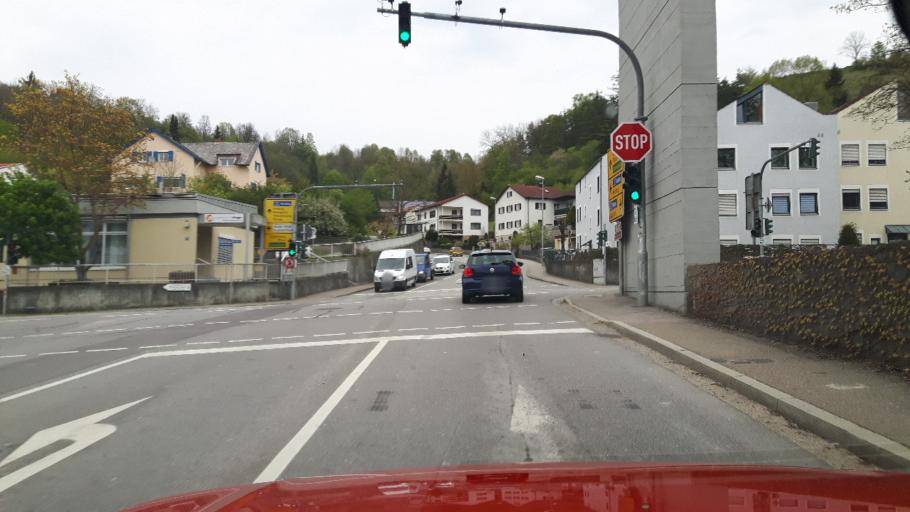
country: DE
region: Bavaria
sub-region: Upper Bavaria
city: Eichstaett
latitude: 48.8854
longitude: 11.2022
